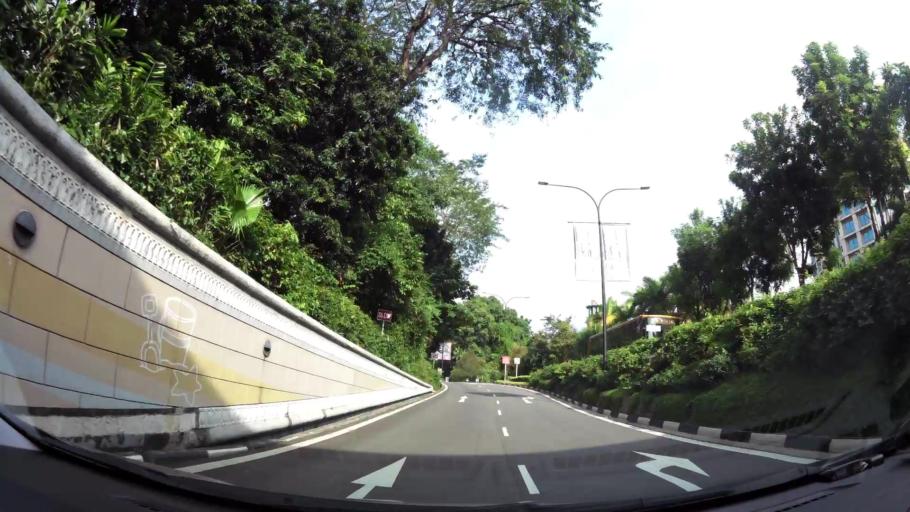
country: SG
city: Singapore
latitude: 1.2546
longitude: 103.8193
